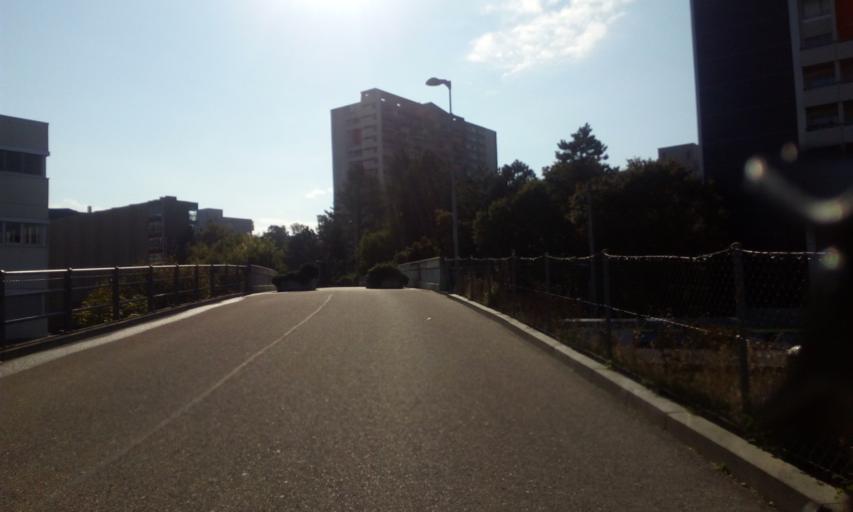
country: CH
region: Bern
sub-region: Bern-Mittelland District
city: Koniz
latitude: 46.9459
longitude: 7.3862
